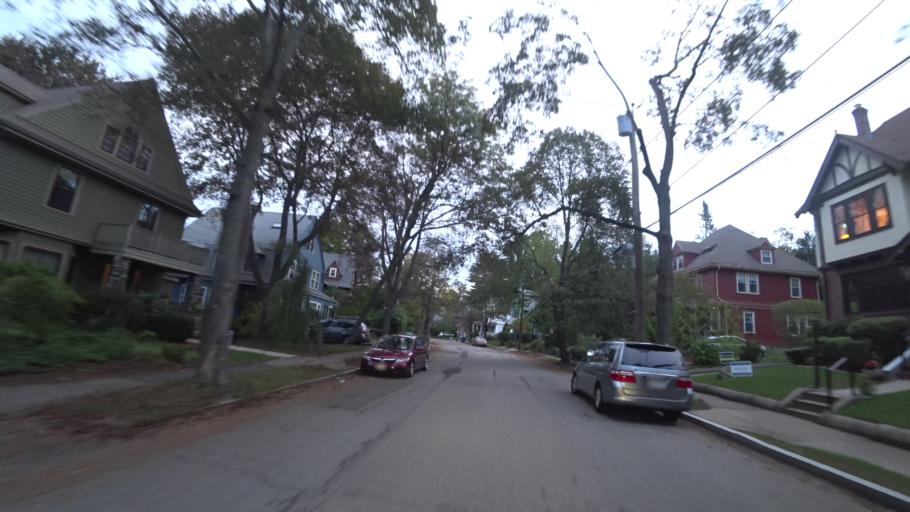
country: US
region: Massachusetts
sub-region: Middlesex County
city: Newton
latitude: 42.3253
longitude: -71.1951
